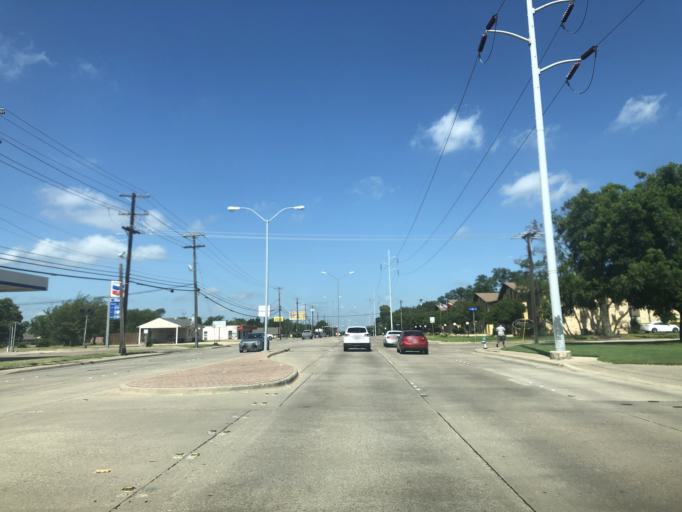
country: US
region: Texas
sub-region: Dallas County
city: Duncanville
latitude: 32.6619
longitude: -96.9134
